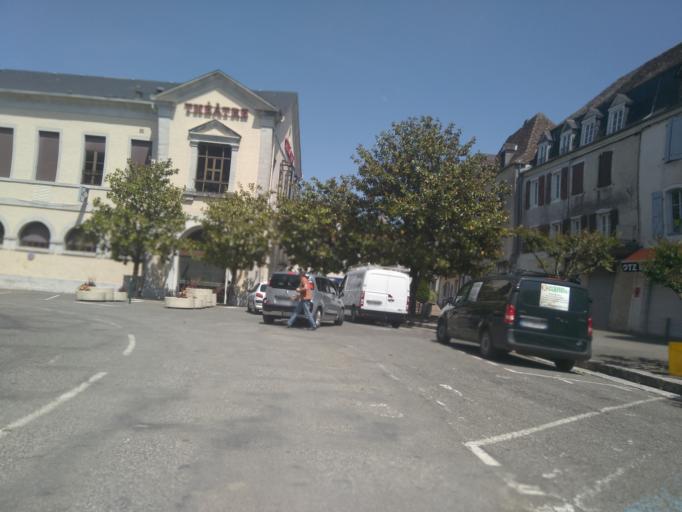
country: FR
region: Aquitaine
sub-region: Departement des Pyrenees-Atlantiques
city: Orthez
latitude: 43.4892
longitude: -0.7750
